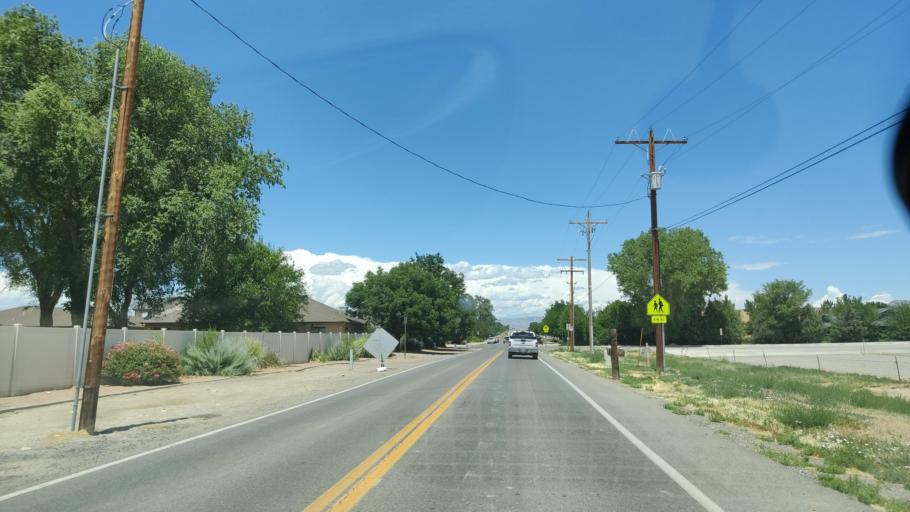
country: US
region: Colorado
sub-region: Mesa County
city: Redlands
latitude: 39.1085
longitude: -108.5988
